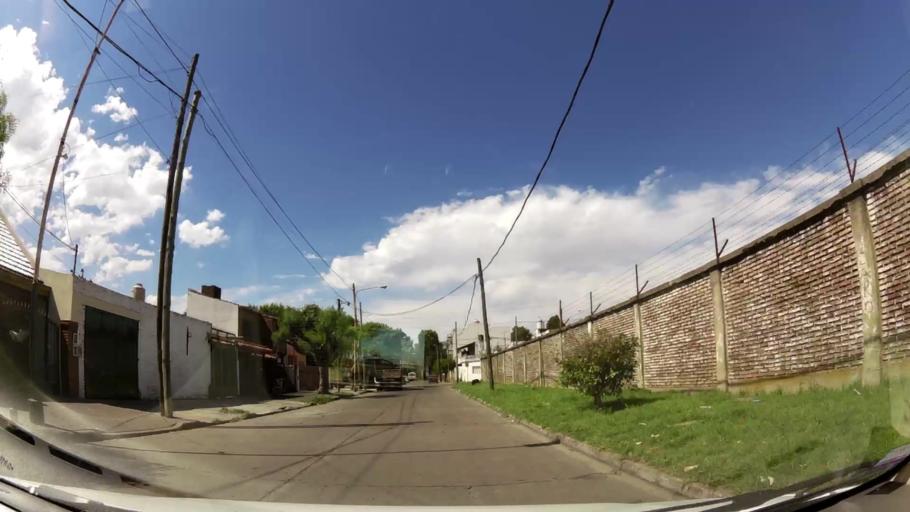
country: AR
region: Buenos Aires
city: San Justo
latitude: -34.6735
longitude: -58.5697
